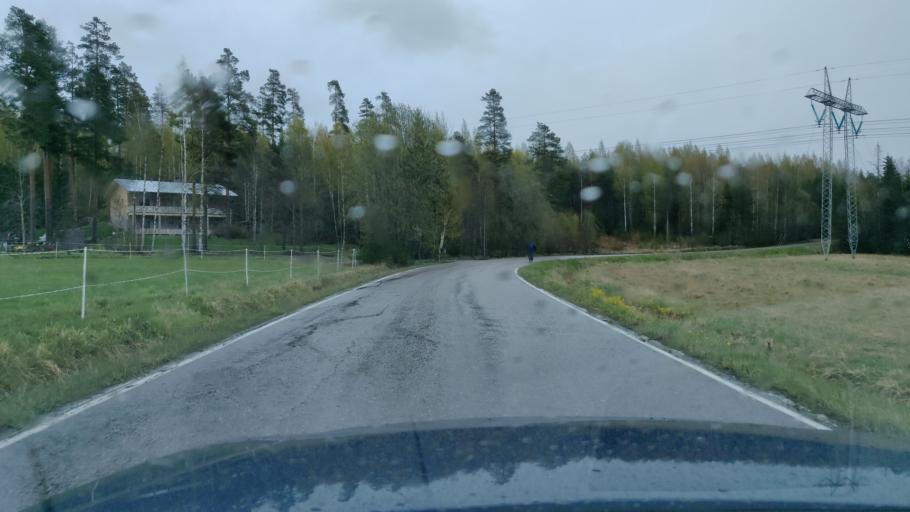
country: FI
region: Uusimaa
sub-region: Helsinki
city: Nurmijaervi
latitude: 60.4834
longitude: 24.7515
